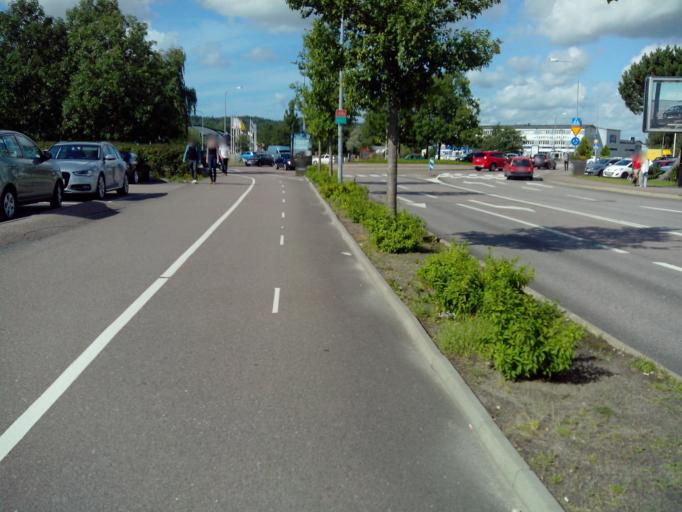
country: SE
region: Vaestra Goetaland
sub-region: Goteborg
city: Goeteborg
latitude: 57.7230
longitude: 11.9516
